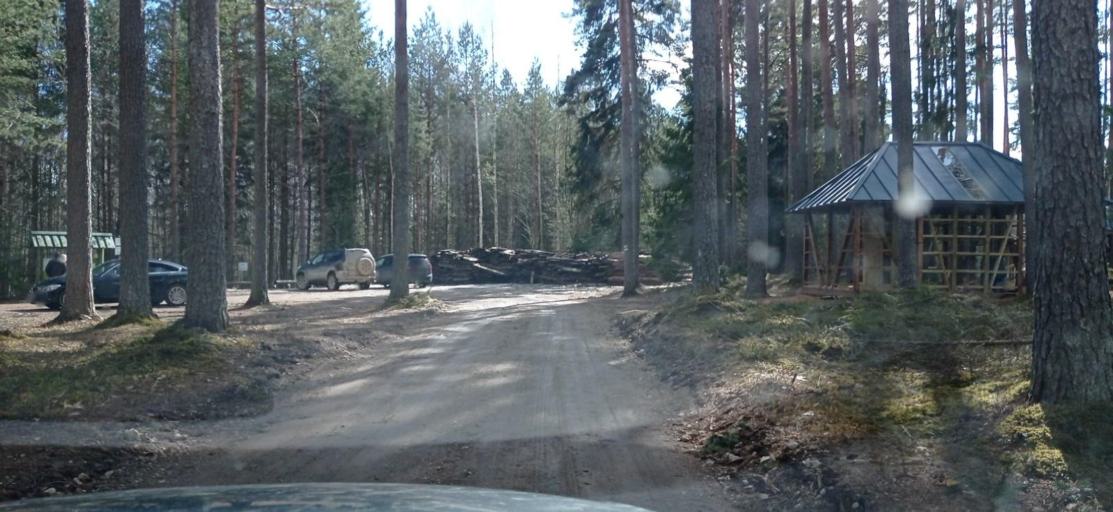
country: EE
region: Polvamaa
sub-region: Polva linn
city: Polva
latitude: 58.1537
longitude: 27.0569
